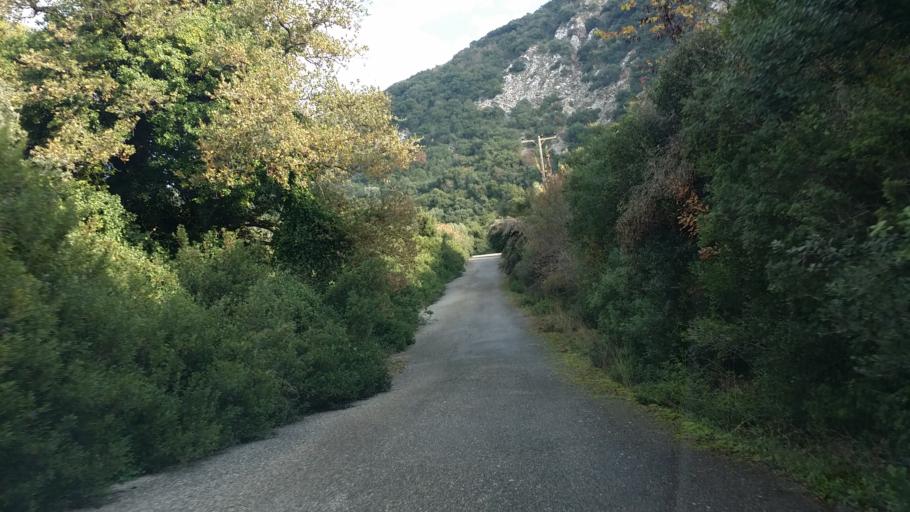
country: GR
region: West Greece
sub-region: Nomos Aitolias kai Akarnanias
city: Katouna
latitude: 38.8511
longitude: 21.0544
